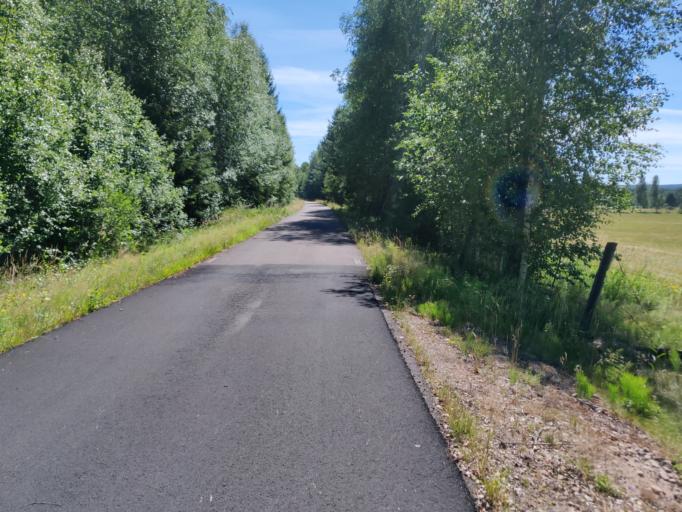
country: SE
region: Vaermland
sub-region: Hagfors Kommun
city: Hagfors
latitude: 59.9698
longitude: 13.5719
